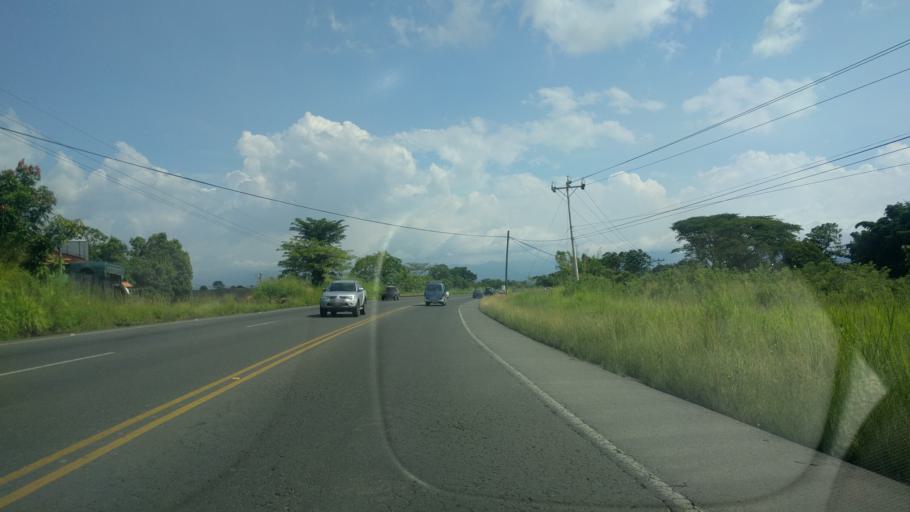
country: CR
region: Alajuela
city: Naranjo
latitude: 10.0371
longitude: -84.3607
